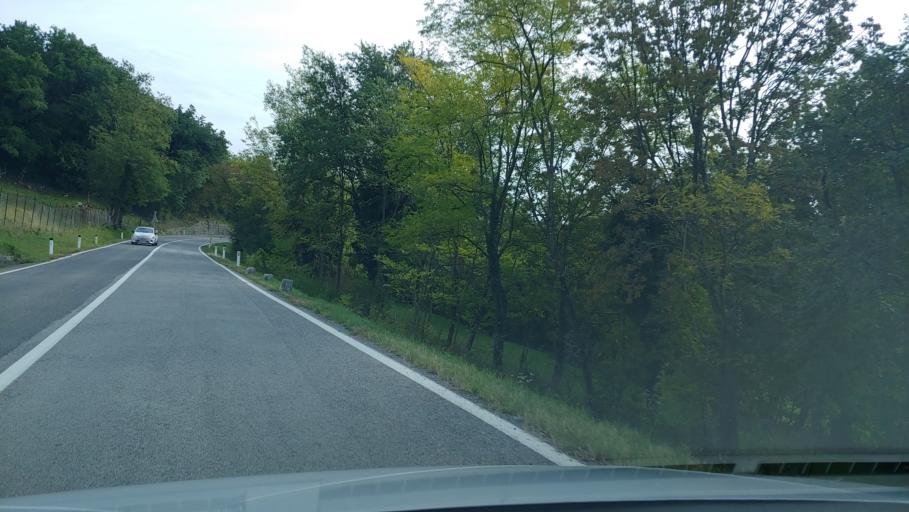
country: SI
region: Nova Gorica
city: Sempas
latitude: 45.9032
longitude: 13.7792
